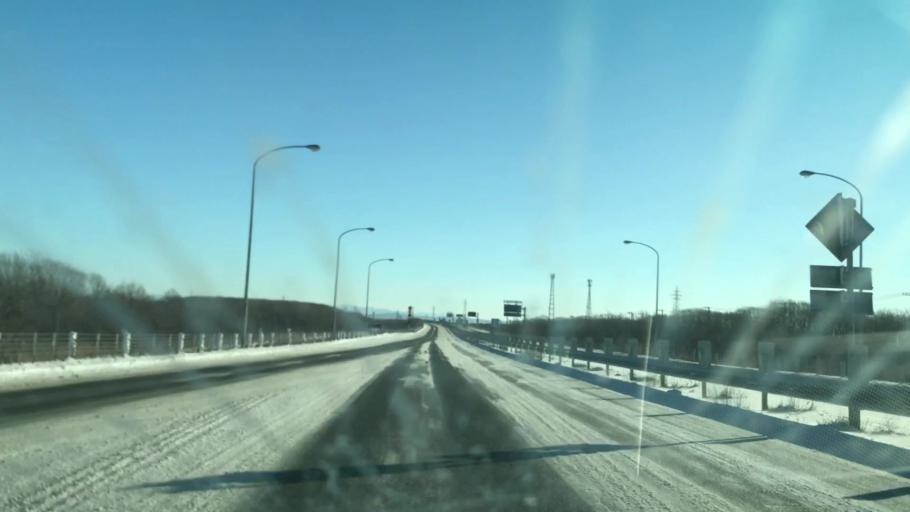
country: JP
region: Hokkaido
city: Tomakomai
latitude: 42.6747
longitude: 141.7359
